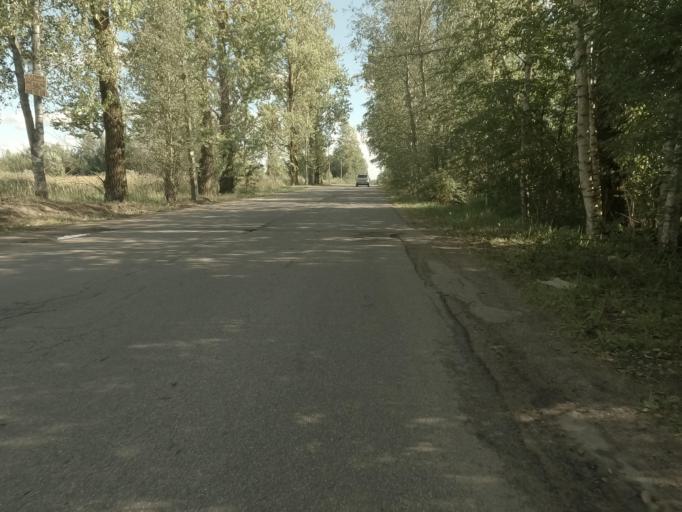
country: RU
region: Leningrad
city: Imeni Morozova
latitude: 59.9684
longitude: 31.0282
